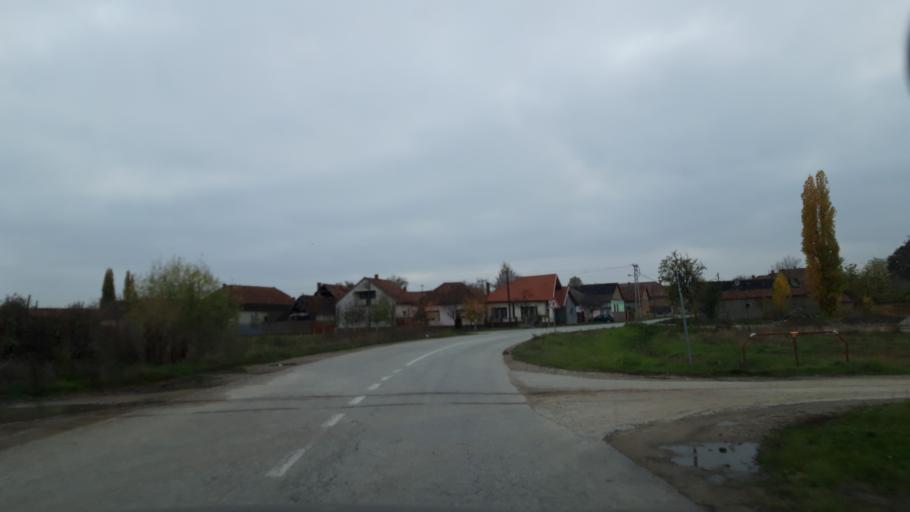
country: RS
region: Autonomna Pokrajina Vojvodina
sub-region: Severnobanatski Okrug
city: Novi Knezevac
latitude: 46.0459
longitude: 20.1038
